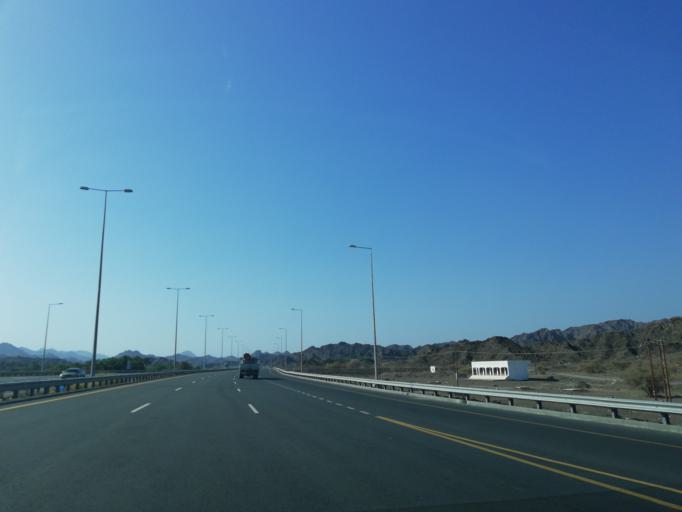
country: OM
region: Muhafazat ad Dakhiliyah
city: Sufalat Sama'il
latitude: 23.0149
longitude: 58.2212
